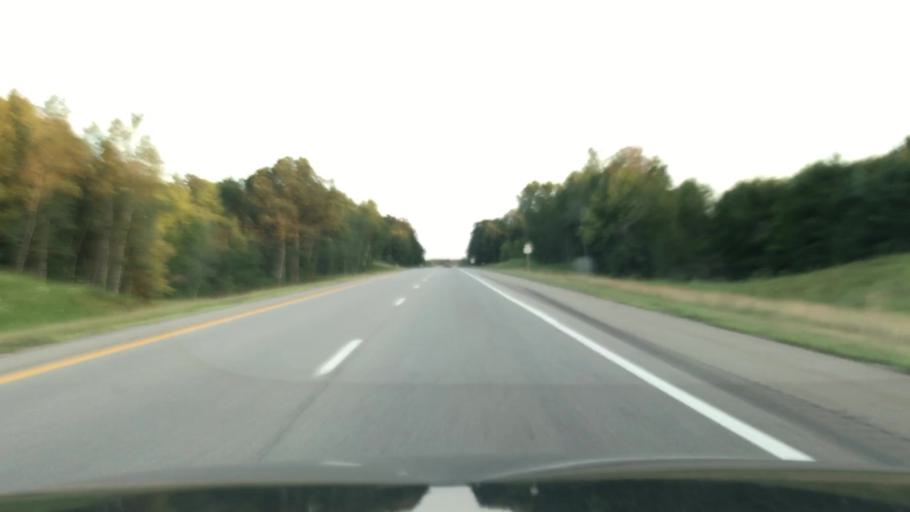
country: US
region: Michigan
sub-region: Montcalm County
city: Howard City
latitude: 43.4825
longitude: -85.4823
